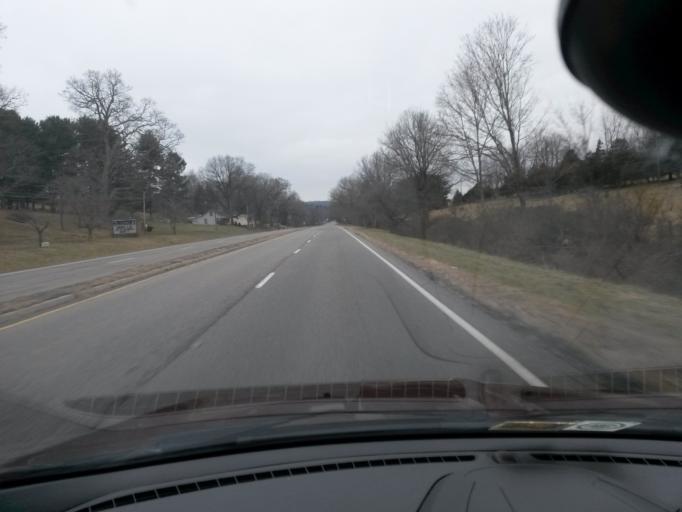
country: US
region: Virginia
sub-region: Augusta County
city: Stuarts Draft
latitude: 37.9303
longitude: -79.1982
